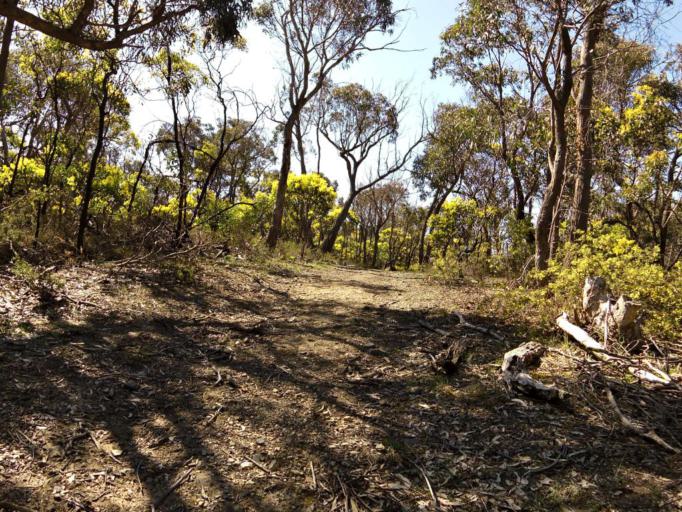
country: AU
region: Victoria
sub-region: Moorabool
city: Bacchus Marsh
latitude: -37.6605
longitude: 144.3190
